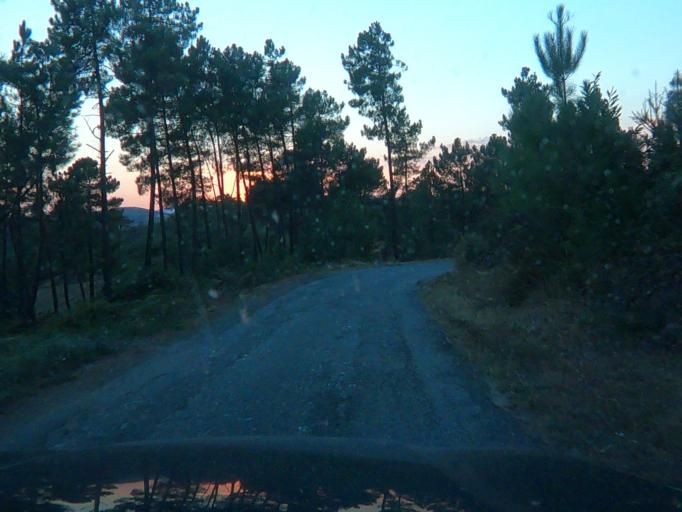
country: PT
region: Vila Real
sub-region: Sabrosa
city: Vilela
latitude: 41.2434
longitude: -7.6219
